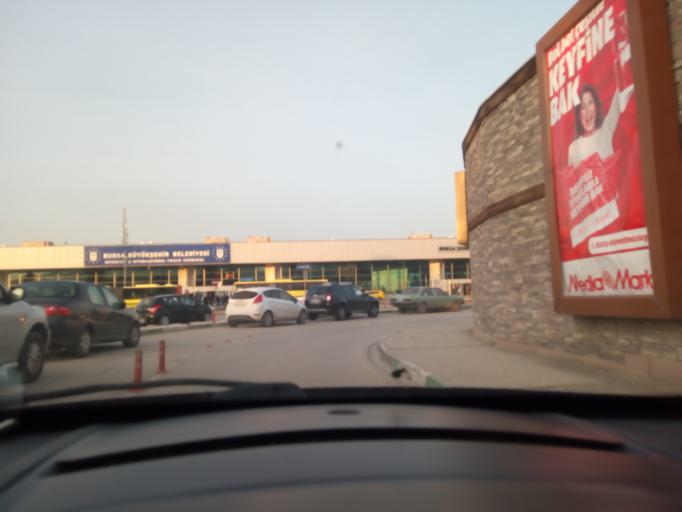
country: TR
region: Bursa
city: Demirtas
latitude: 40.2658
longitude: 29.0544
